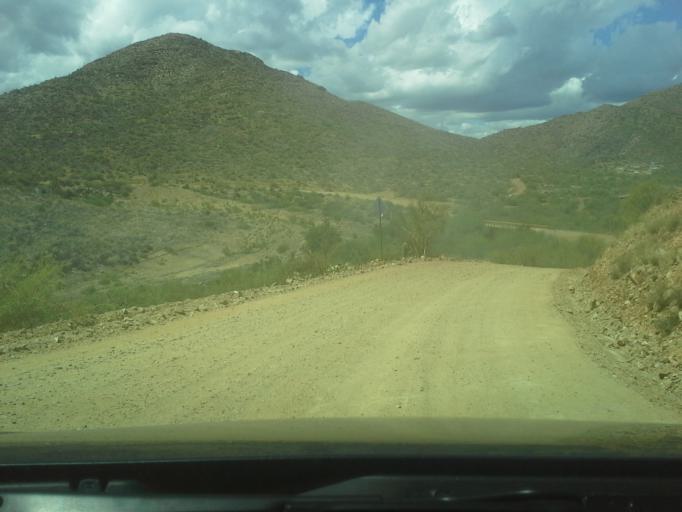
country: US
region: Arizona
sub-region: Yavapai County
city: Spring Valley
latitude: 34.2726
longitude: -112.2012
